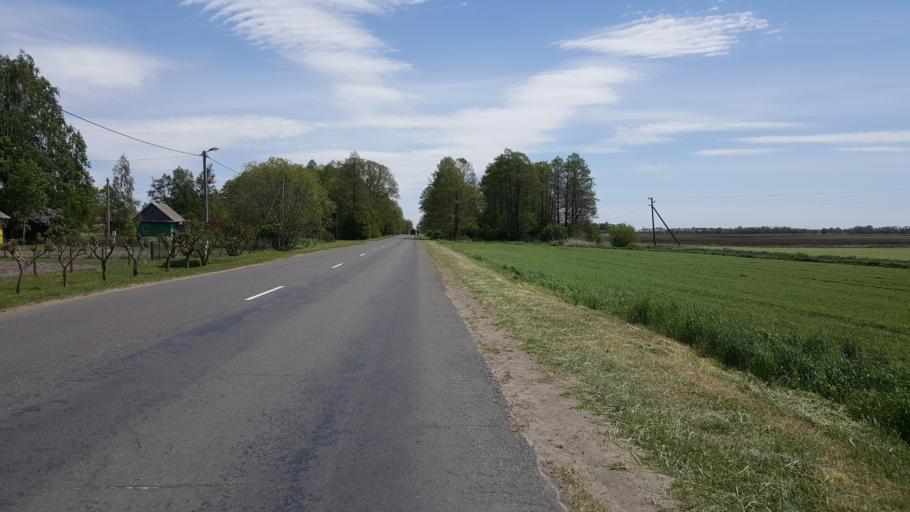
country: BY
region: Brest
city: Kobryn
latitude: 52.3457
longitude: 24.2163
